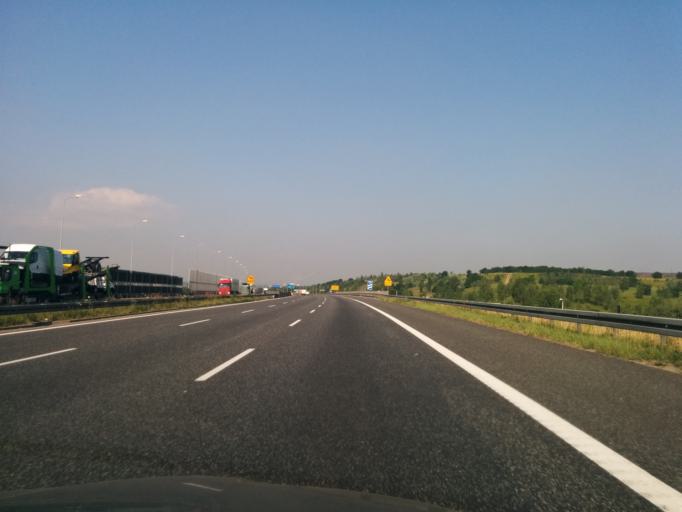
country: PL
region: Silesian Voivodeship
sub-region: Powiat gliwicki
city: Przyszowice
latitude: 50.2696
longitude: 18.7593
